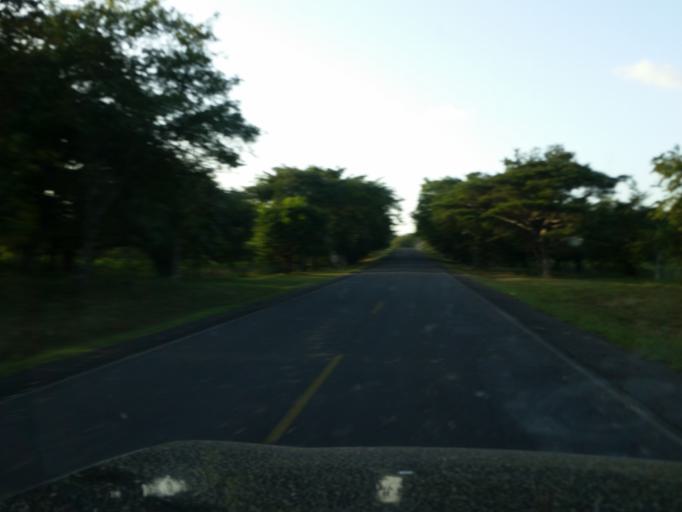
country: NI
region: Rio San Juan
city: El Almendro
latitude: 11.6046
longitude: -84.8637
